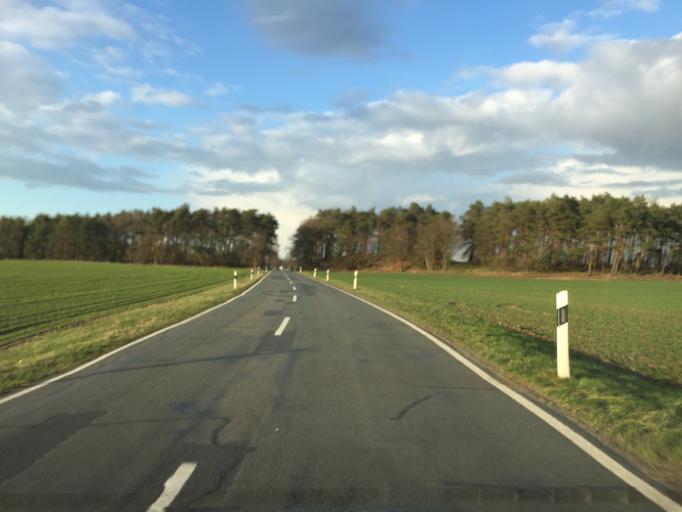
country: DE
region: Lower Saxony
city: Steyerberg
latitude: 52.5847
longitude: 8.9793
